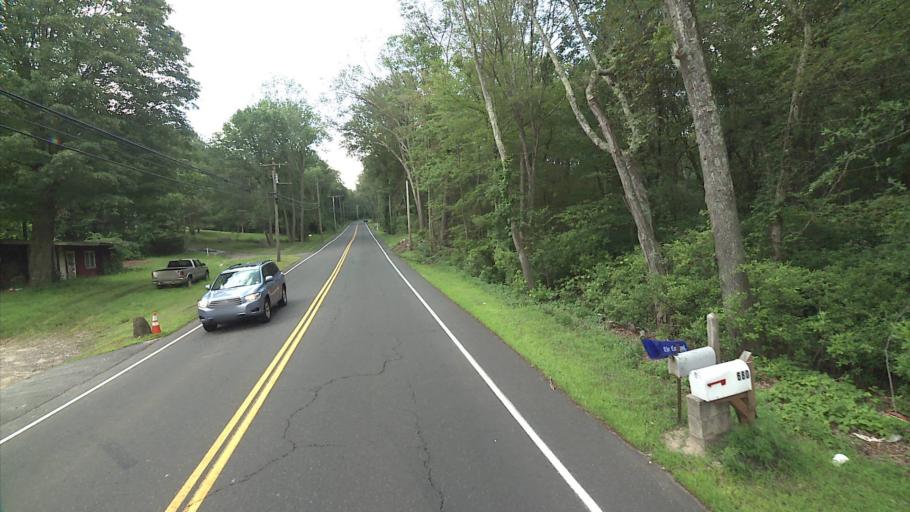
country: US
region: Connecticut
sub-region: Middlesex County
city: Higganum
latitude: 41.4513
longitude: -72.5552
